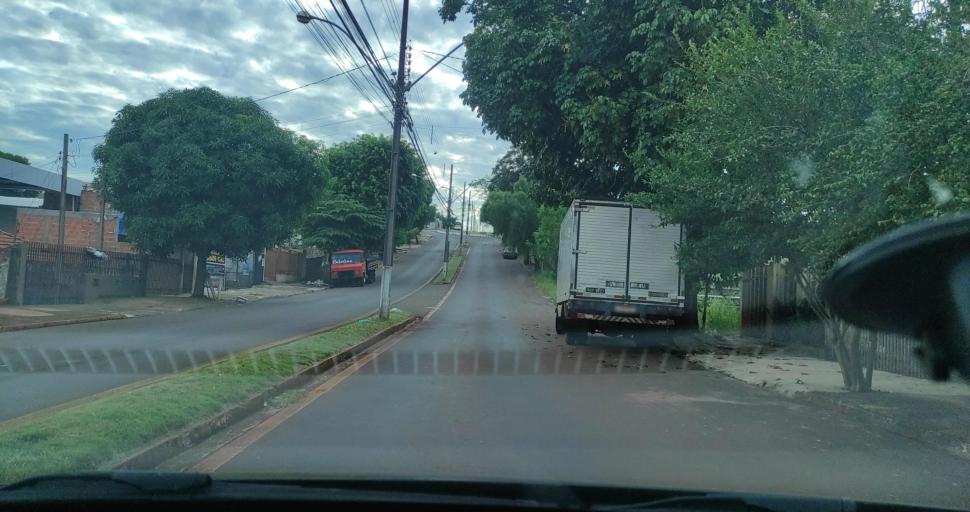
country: BR
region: Parana
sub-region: Ibipora
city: Ibipora
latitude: -23.2663
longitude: -51.0418
